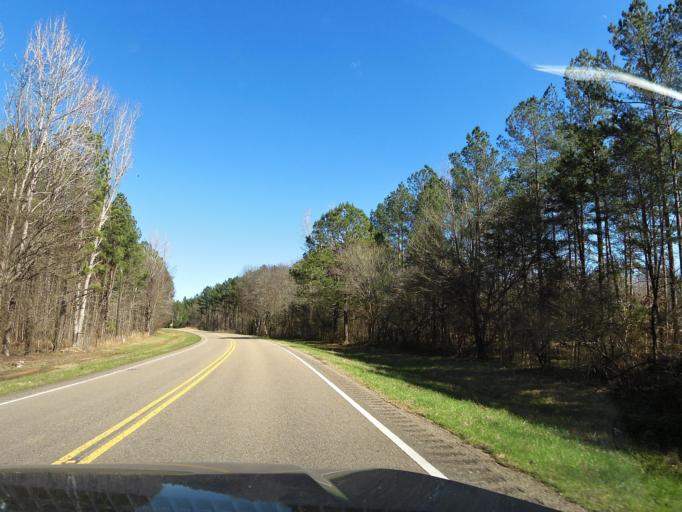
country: US
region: Alabama
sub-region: Bullock County
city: Union Springs
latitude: 32.1118
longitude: -85.7885
